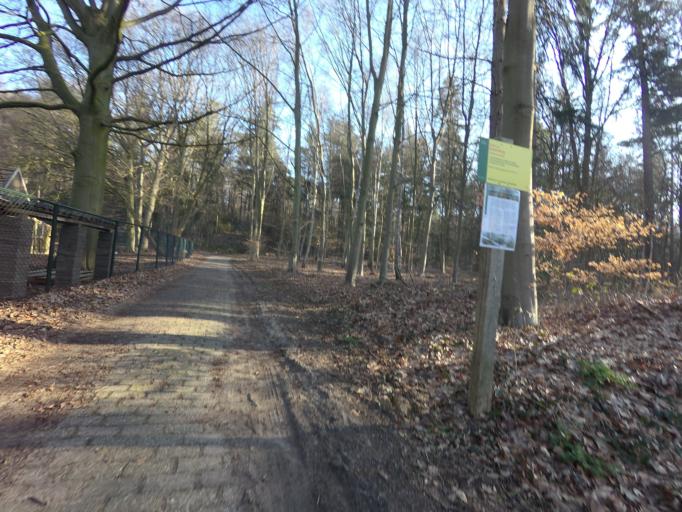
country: NL
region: Gelderland
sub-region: Gemeente Lochem
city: Barchem
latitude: 52.1298
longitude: 6.4354
